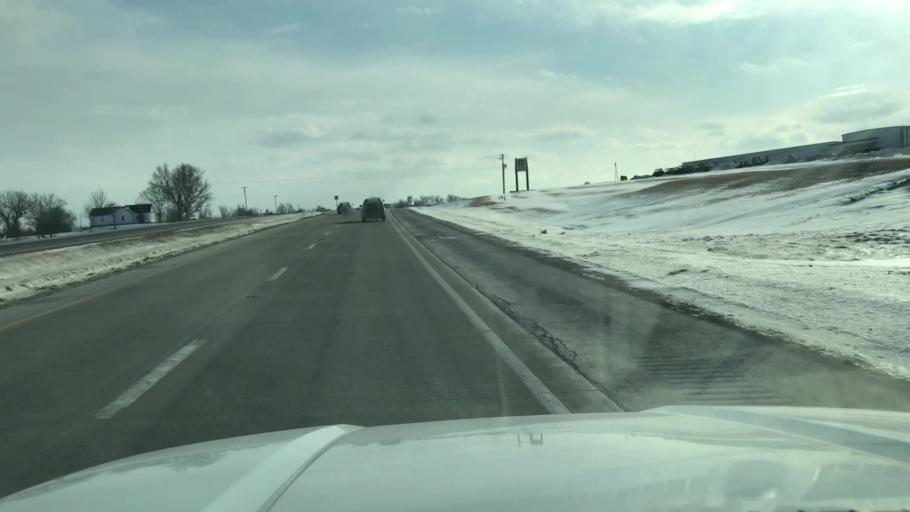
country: US
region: Missouri
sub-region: Nodaway County
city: Maryville
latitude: 40.3022
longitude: -94.8749
